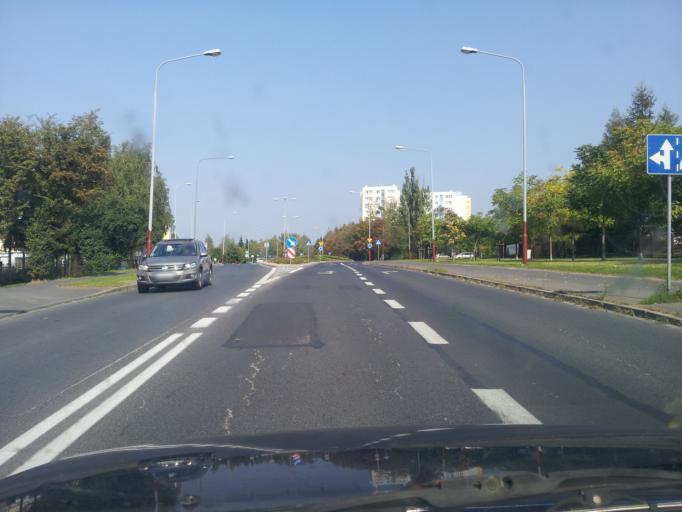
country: PL
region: Greater Poland Voivodeship
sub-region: Powiat poznanski
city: Suchy Las
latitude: 52.4586
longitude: 16.9042
